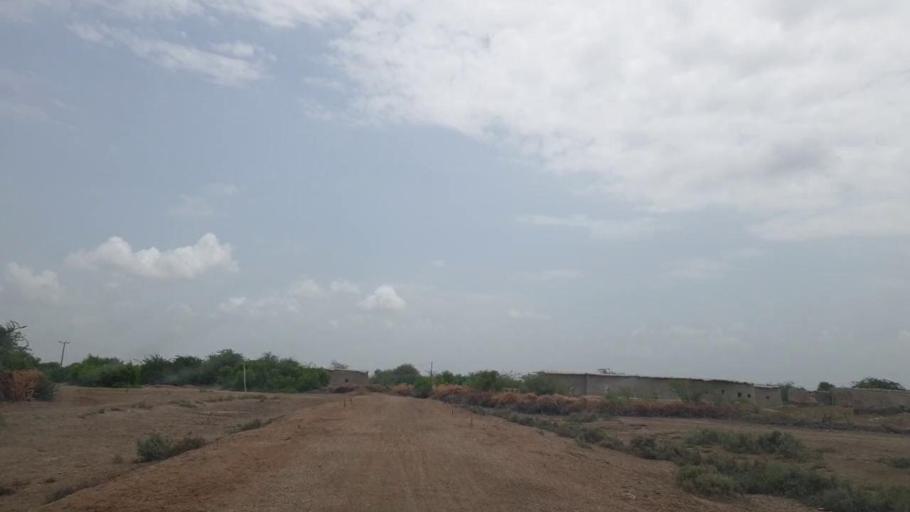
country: PK
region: Sindh
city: Naukot
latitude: 24.8969
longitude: 69.2028
